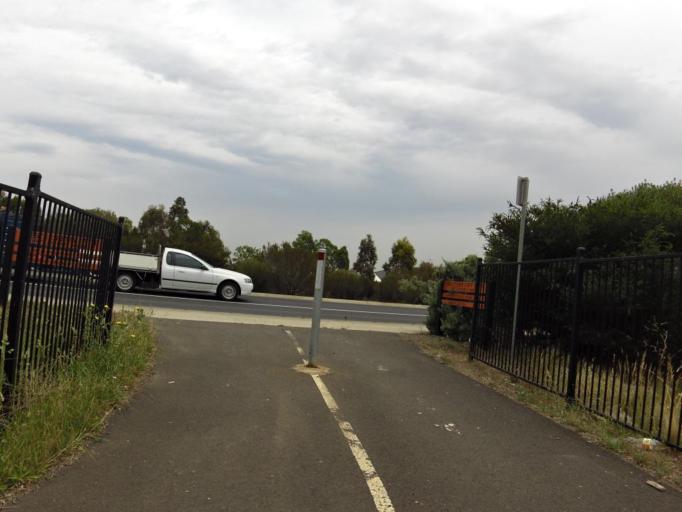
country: AU
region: Victoria
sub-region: Brimbank
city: Derrimut
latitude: -37.7963
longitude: 144.7714
